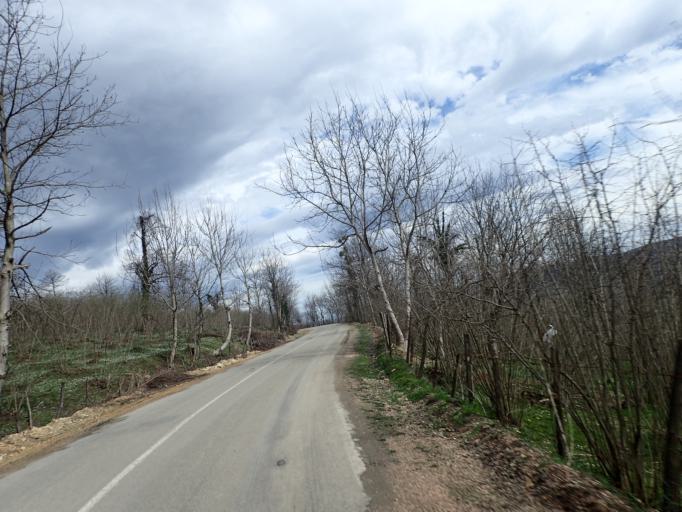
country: TR
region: Ordu
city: Kumru
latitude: 40.9359
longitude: 37.2612
